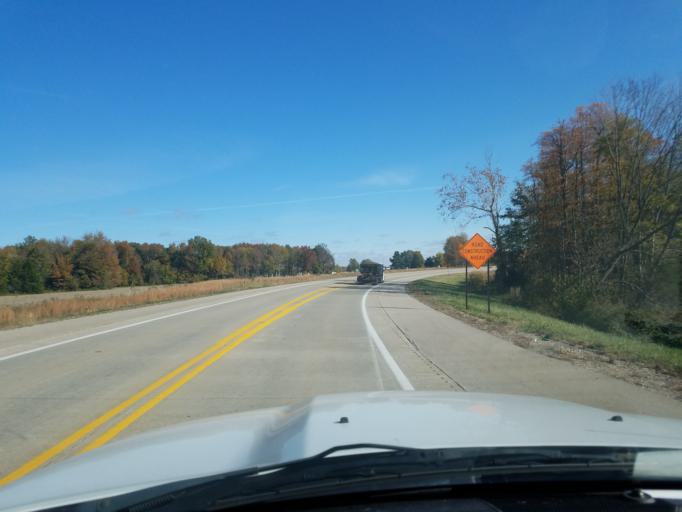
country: US
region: Indiana
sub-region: Jennings County
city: North Vernon
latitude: 39.0316
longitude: -85.6457
